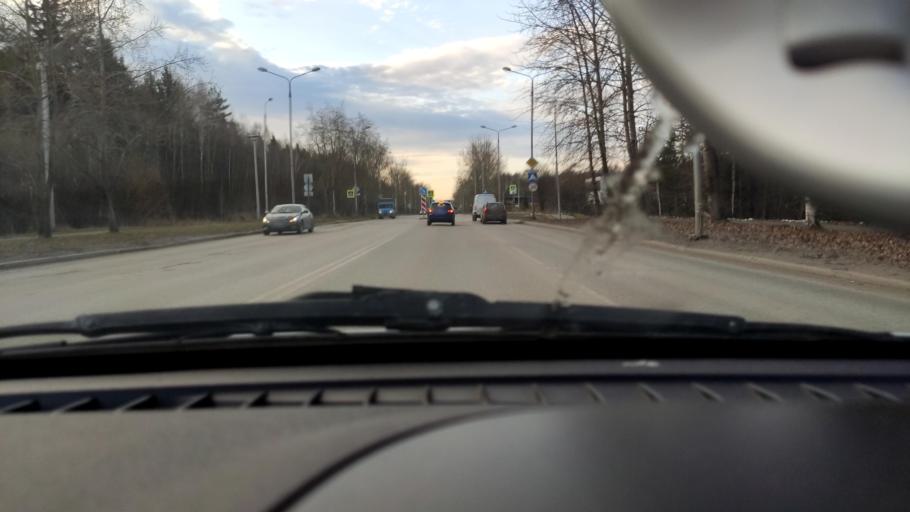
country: RU
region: Perm
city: Perm
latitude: 58.0840
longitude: 56.3766
